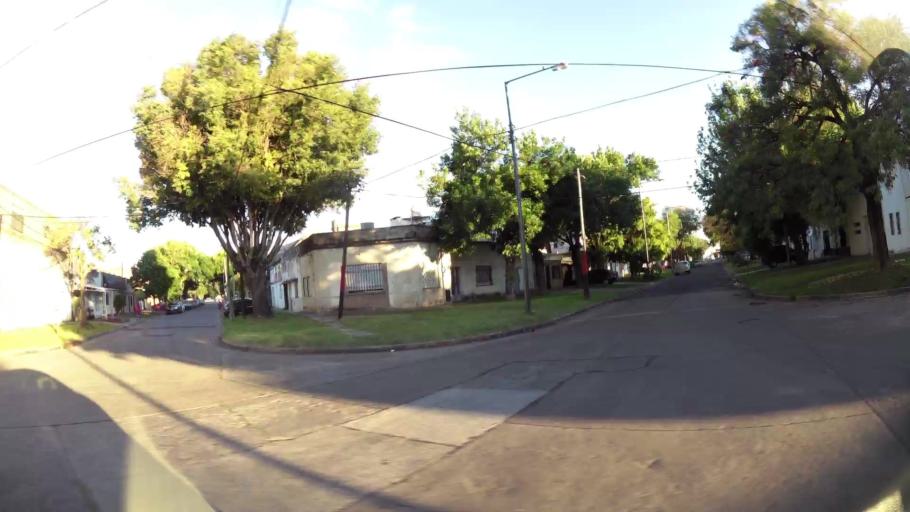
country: AR
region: Santa Fe
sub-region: Departamento de Rosario
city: Rosario
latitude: -32.9713
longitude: -60.6701
